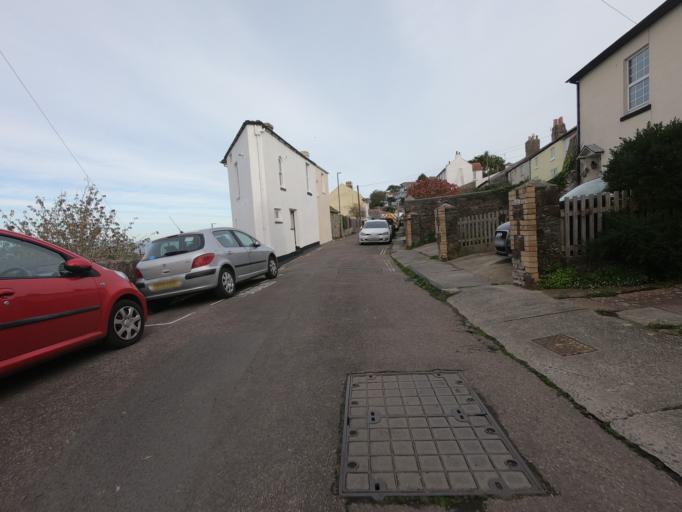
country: GB
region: England
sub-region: Borough of Torbay
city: Brixham
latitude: 50.3945
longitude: -3.5137
